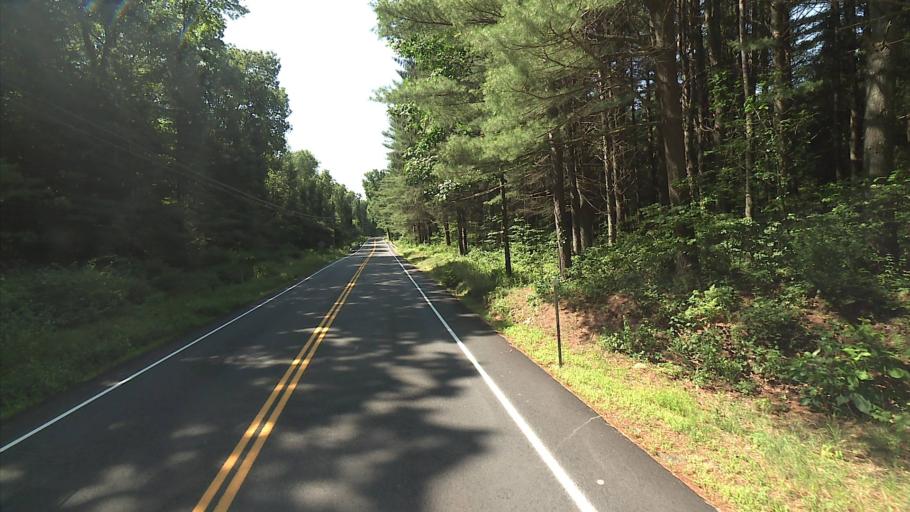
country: US
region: Connecticut
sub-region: Litchfield County
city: Terryville
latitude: 41.7312
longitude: -73.0145
